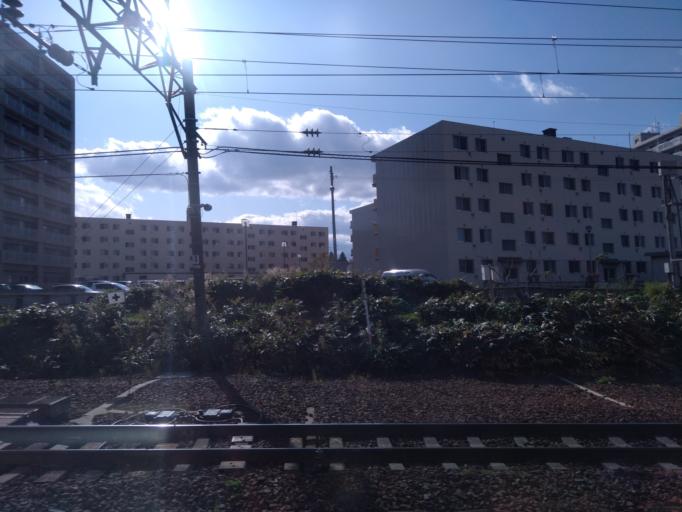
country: JP
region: Hokkaido
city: Sapporo
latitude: 43.0578
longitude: 141.4089
